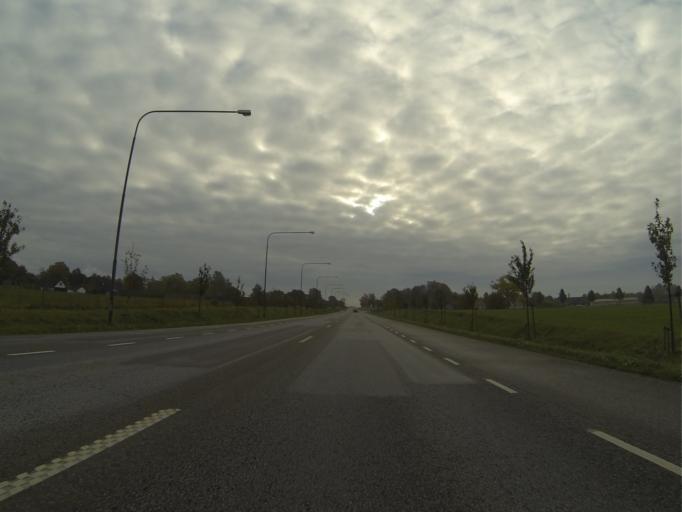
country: SE
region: Skane
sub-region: Tomelilla Kommun
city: Tomelilla
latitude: 55.5530
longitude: 13.9368
